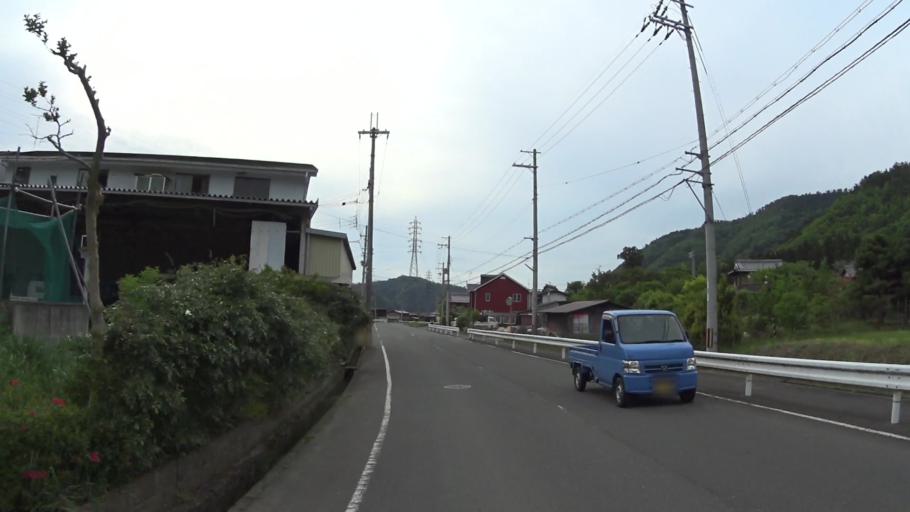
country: JP
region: Kyoto
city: Kameoka
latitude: 35.1029
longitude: 135.5299
